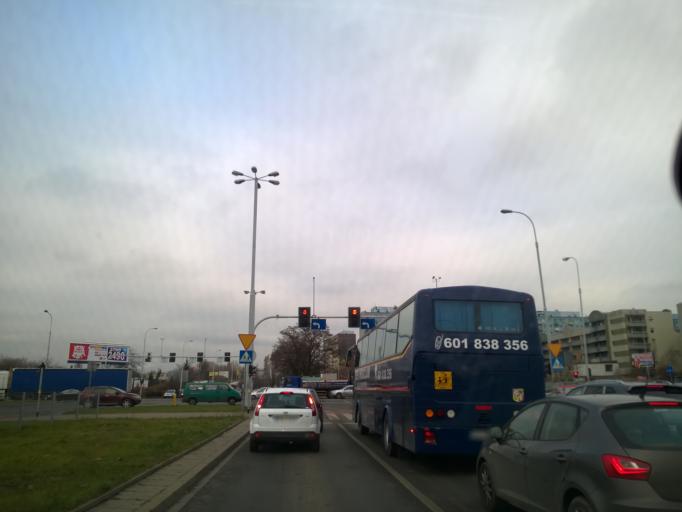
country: PL
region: Lower Silesian Voivodeship
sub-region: Powiat wroclawski
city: Wroclaw
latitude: 51.0827
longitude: 17.0348
